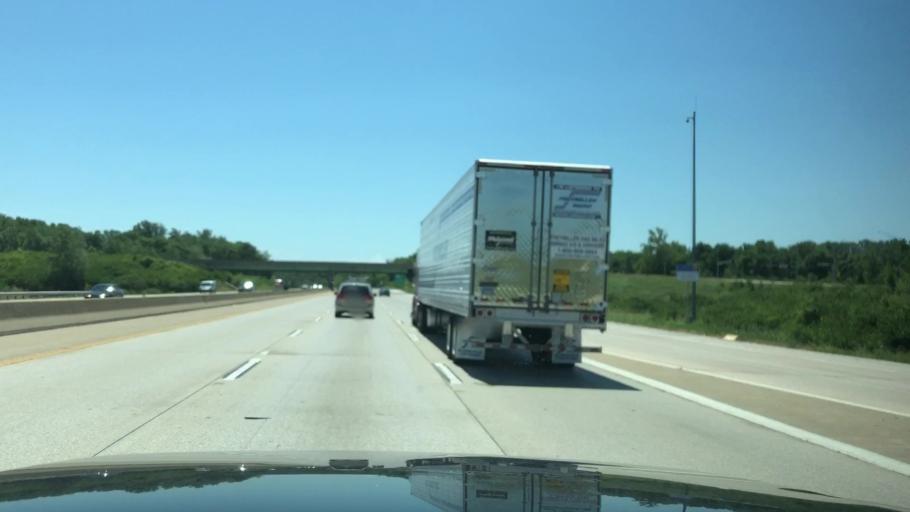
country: US
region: Missouri
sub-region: Saint Louis County
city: Bridgeton
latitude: 38.7826
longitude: -90.4179
